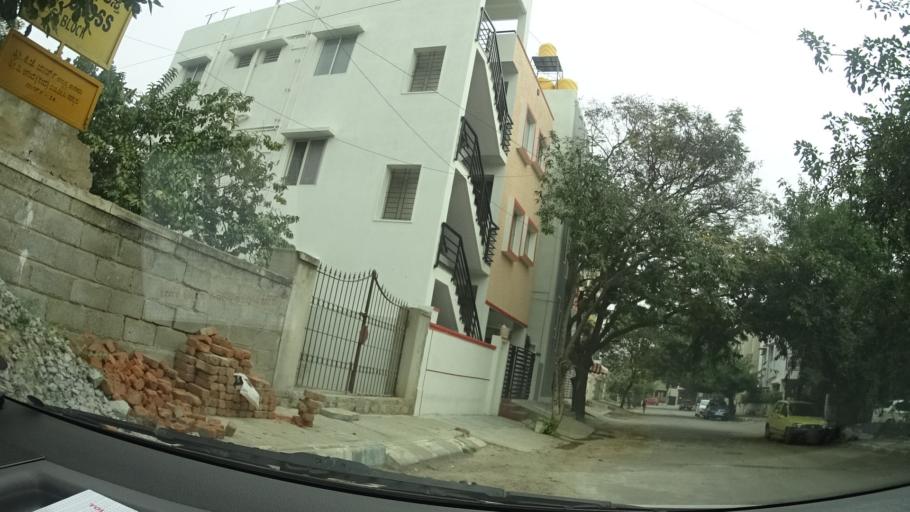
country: IN
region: Karnataka
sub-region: Bangalore Urban
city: Yelahanka
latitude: 13.0386
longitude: 77.6284
